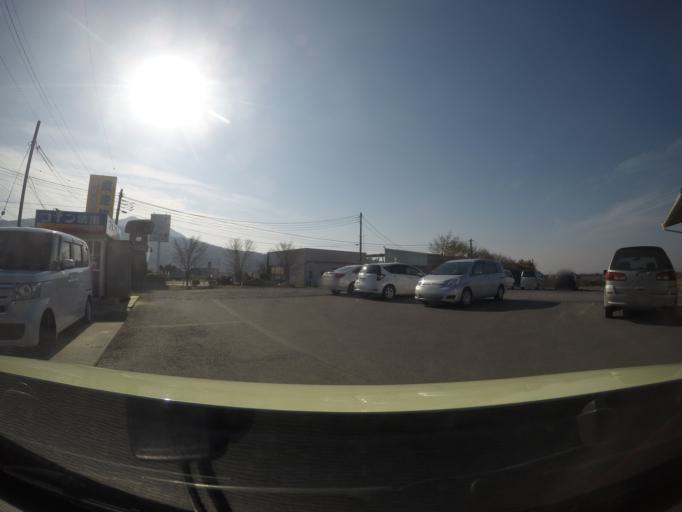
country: JP
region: Ibaraki
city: Makabe
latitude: 36.2707
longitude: 140.1050
